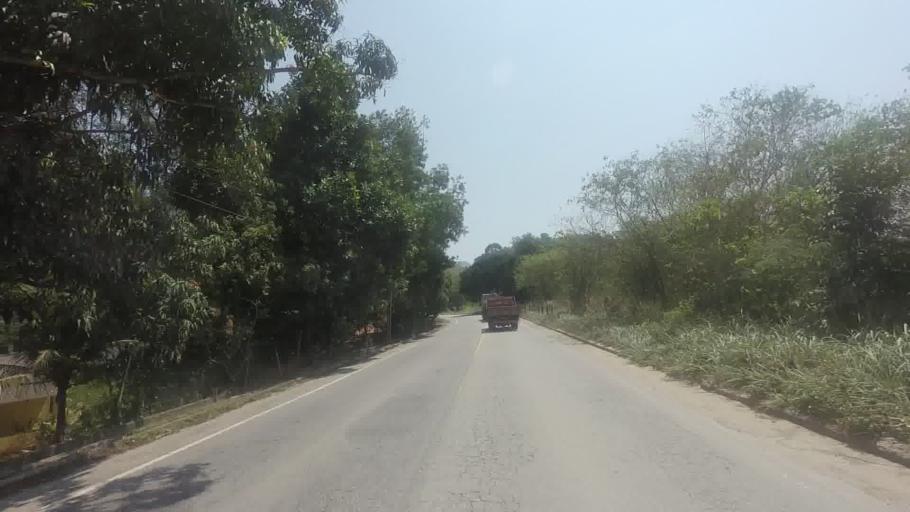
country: BR
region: Espirito Santo
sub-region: Rio Novo Do Sul
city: Rio Novo do Sul
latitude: -20.8717
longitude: -41.0198
